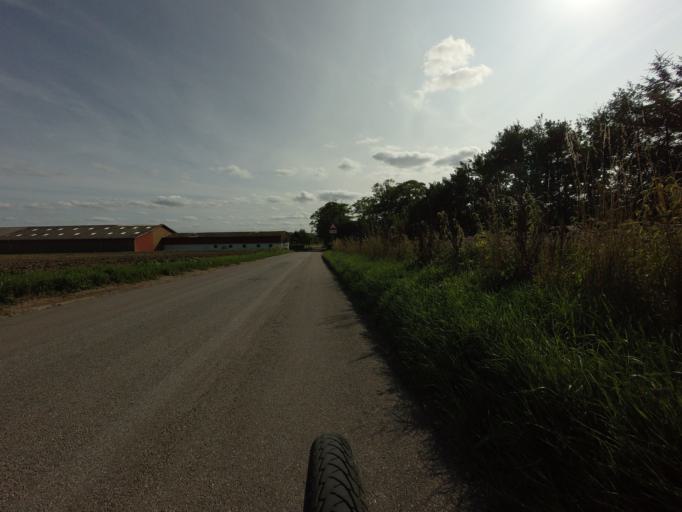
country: DK
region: Zealand
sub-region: Faxe Kommune
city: Fakse
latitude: 55.1880
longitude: 12.1131
